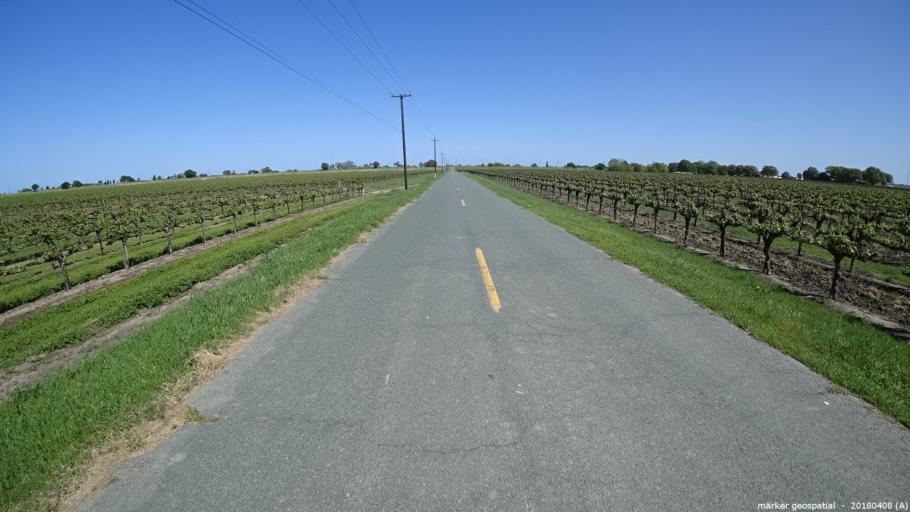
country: US
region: California
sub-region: Sacramento County
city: Walnut Grove
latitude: 38.3134
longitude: -121.5250
